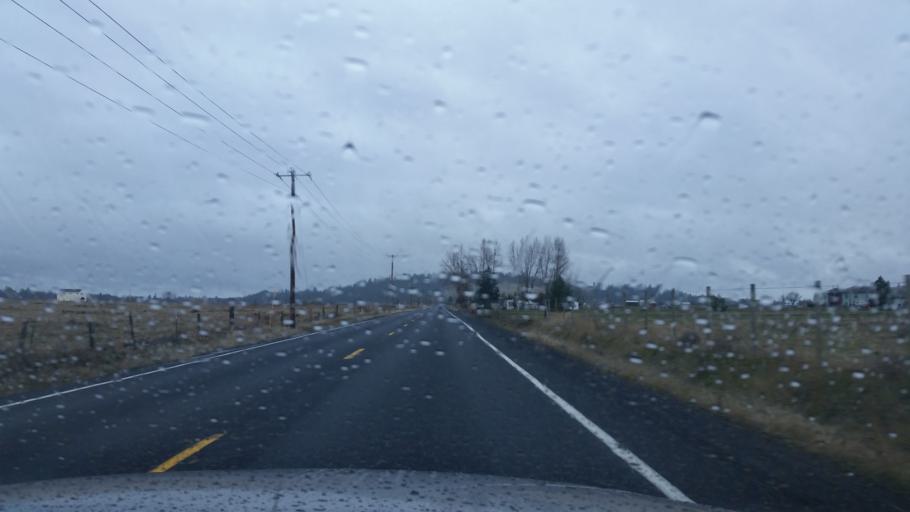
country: US
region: Washington
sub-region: Spokane County
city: Fairchild Air Force Base
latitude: 47.5763
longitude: -117.6076
